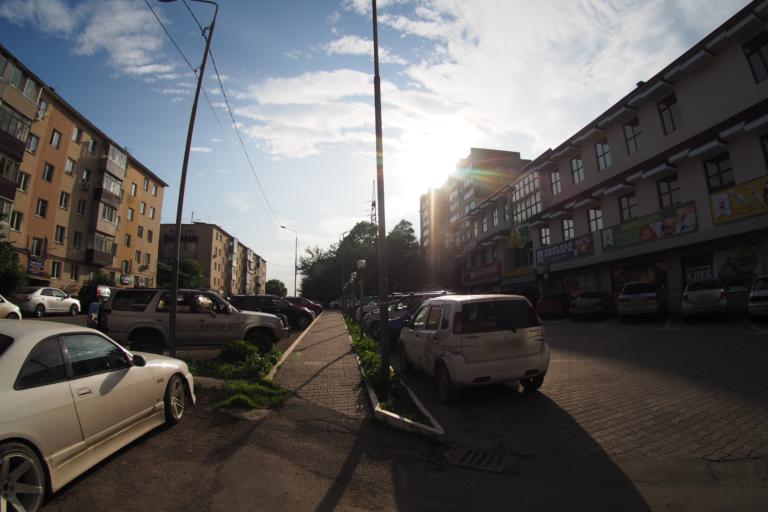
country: RU
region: Primorskiy
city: Vladivostok
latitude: 43.1126
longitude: 131.9292
